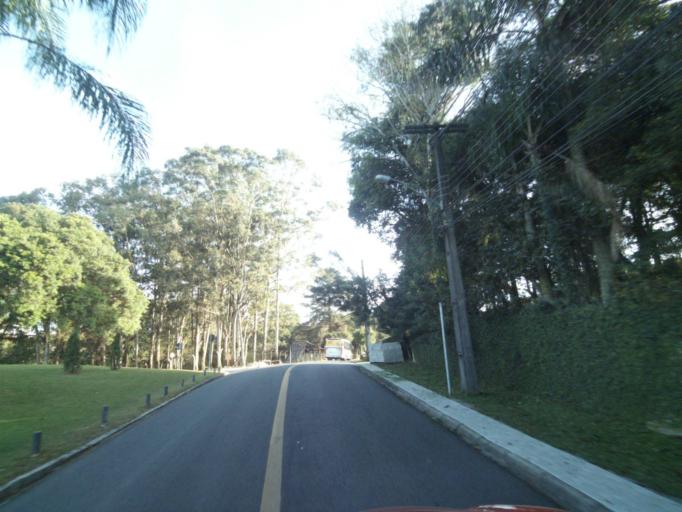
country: BR
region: Parana
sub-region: Curitiba
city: Curitiba
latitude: -25.4302
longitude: -49.3024
